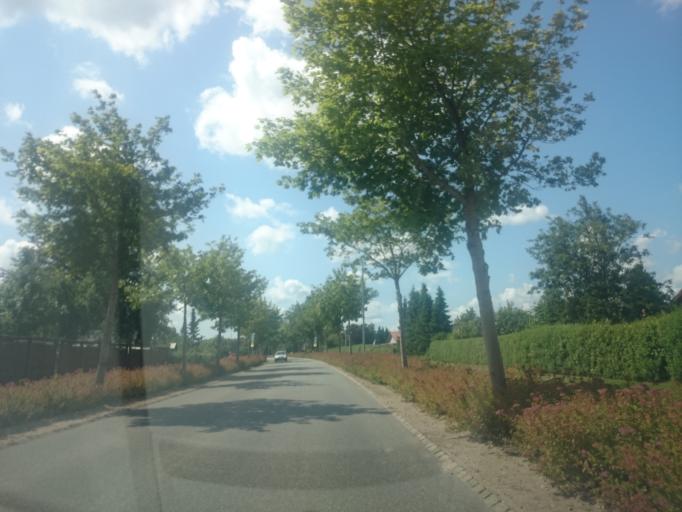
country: DK
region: South Denmark
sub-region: Billund Kommune
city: Billund
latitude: 55.7311
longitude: 9.1052
